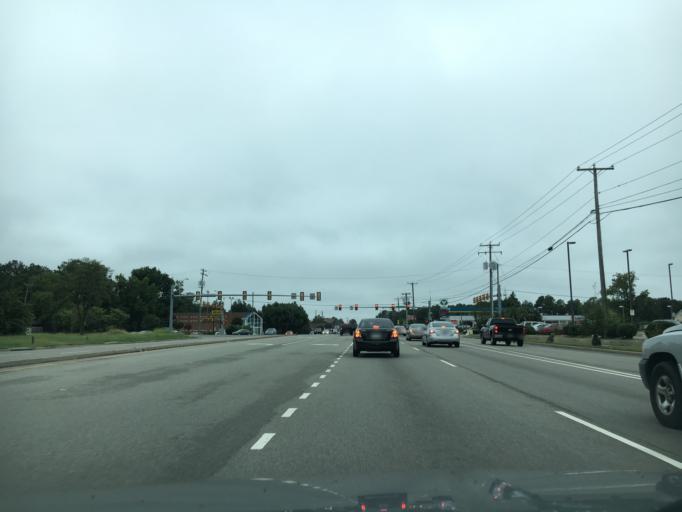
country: US
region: Virginia
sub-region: Chesterfield County
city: Bensley
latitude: 37.4935
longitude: -77.4872
